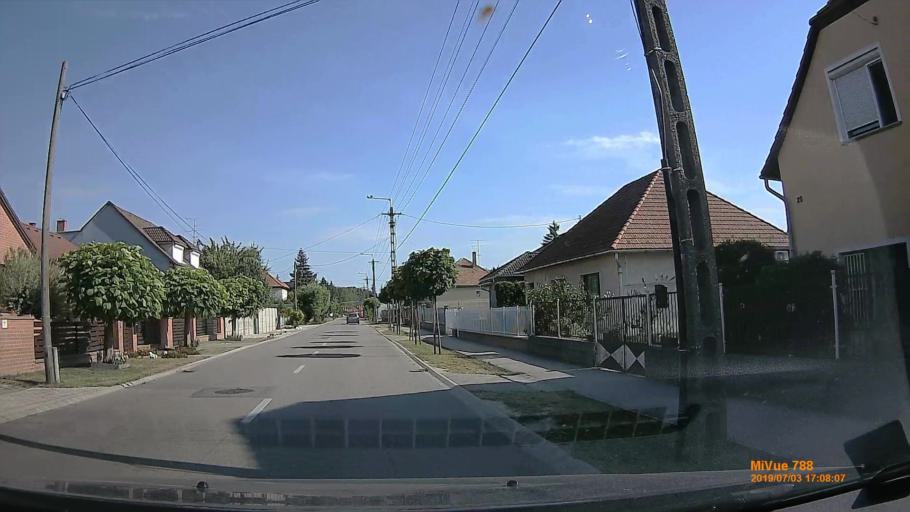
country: HU
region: Gyor-Moson-Sopron
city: Gyor
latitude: 47.7163
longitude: 17.6511
